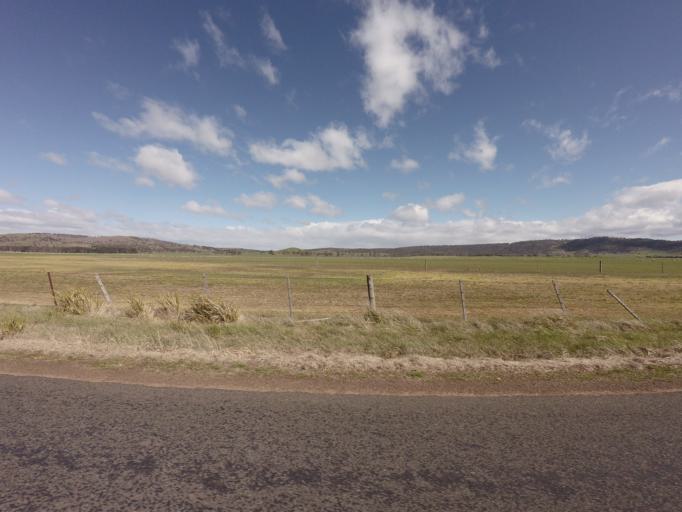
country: AU
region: Tasmania
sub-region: Northern Midlands
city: Evandale
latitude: -42.0170
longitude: 147.4650
